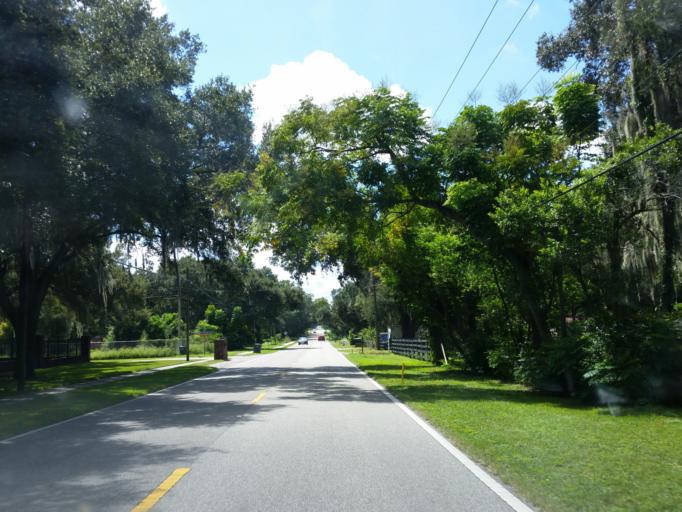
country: US
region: Florida
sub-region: Hillsborough County
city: Brandon
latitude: 27.9004
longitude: -82.2857
